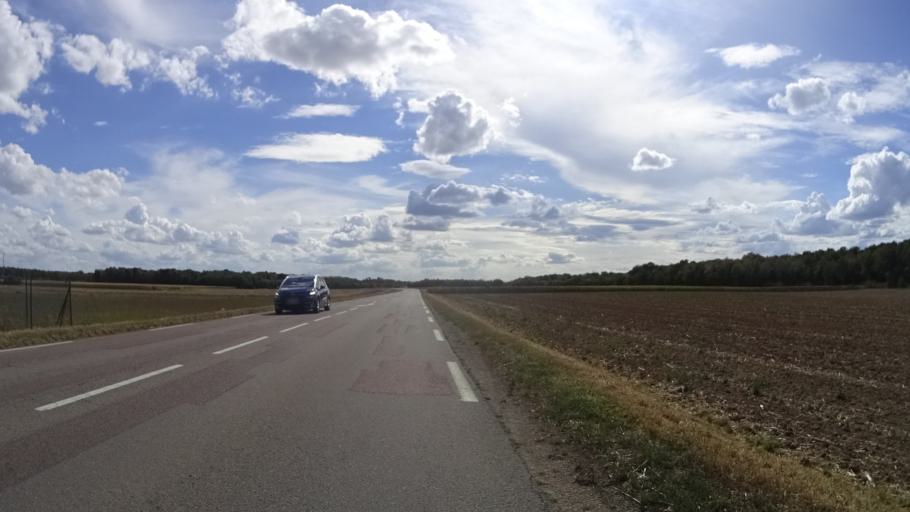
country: FR
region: Bourgogne
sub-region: Departement de la Cote-d'Or
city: Seurre
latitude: 47.0438
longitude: 5.1912
